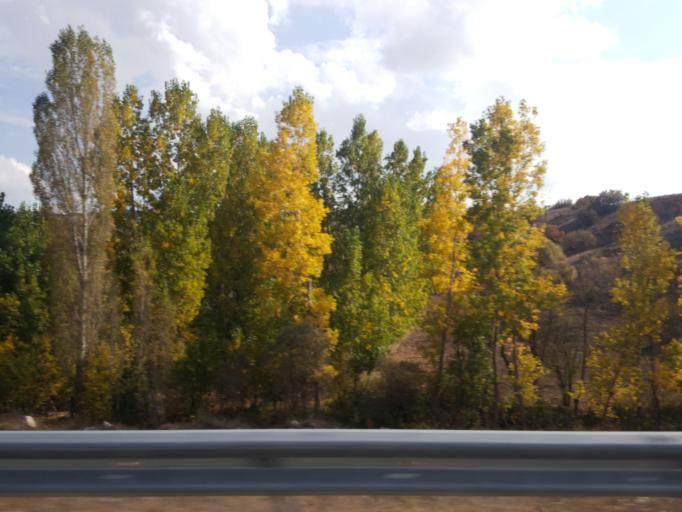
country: TR
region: Corum
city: Alaca
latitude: 40.3321
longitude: 34.7097
